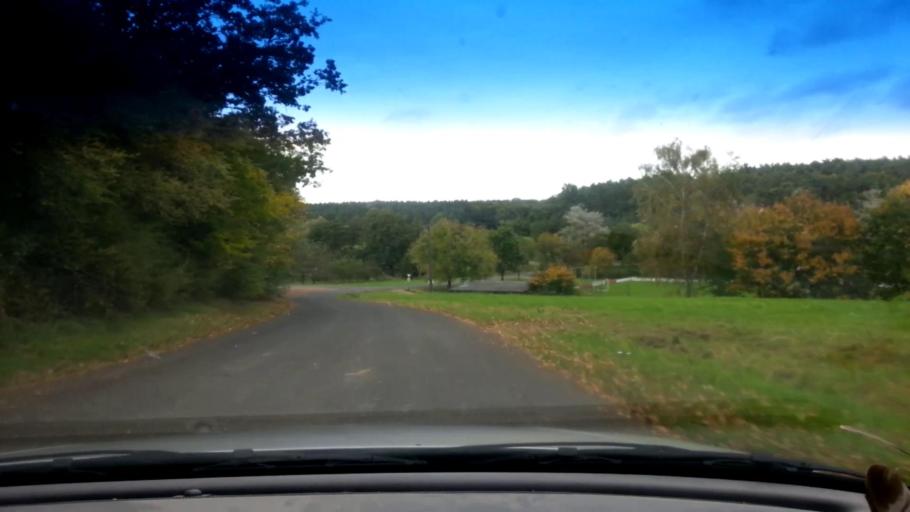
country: DE
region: Bavaria
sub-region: Upper Franconia
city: Gerach
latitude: 50.0335
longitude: 10.8011
